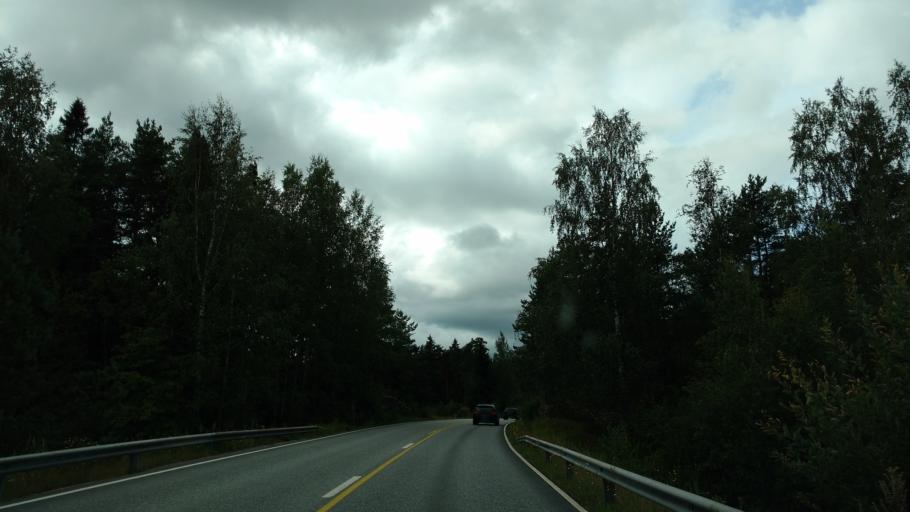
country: FI
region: Varsinais-Suomi
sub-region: Aboland-Turunmaa
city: Kimito
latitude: 60.1404
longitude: 22.6747
